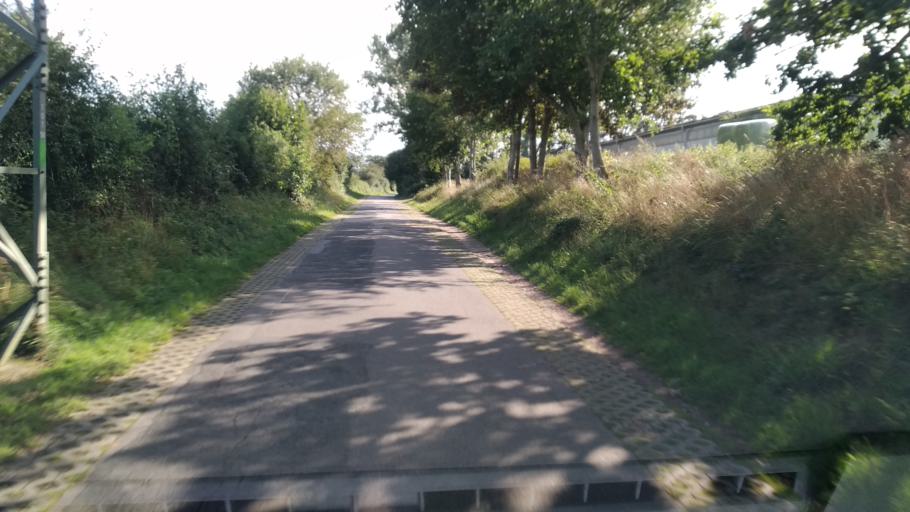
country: DE
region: Schleswig-Holstein
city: Busdorf
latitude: 54.4849
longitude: 9.5427
